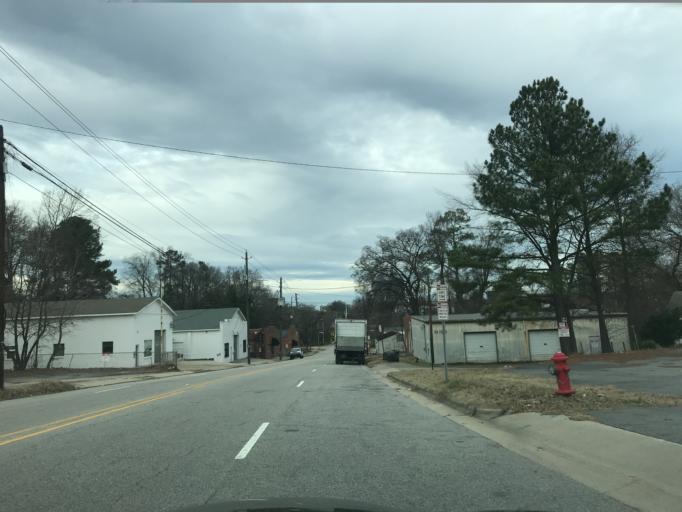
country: US
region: North Carolina
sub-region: Wake County
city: Raleigh
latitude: 35.7673
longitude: -78.6489
